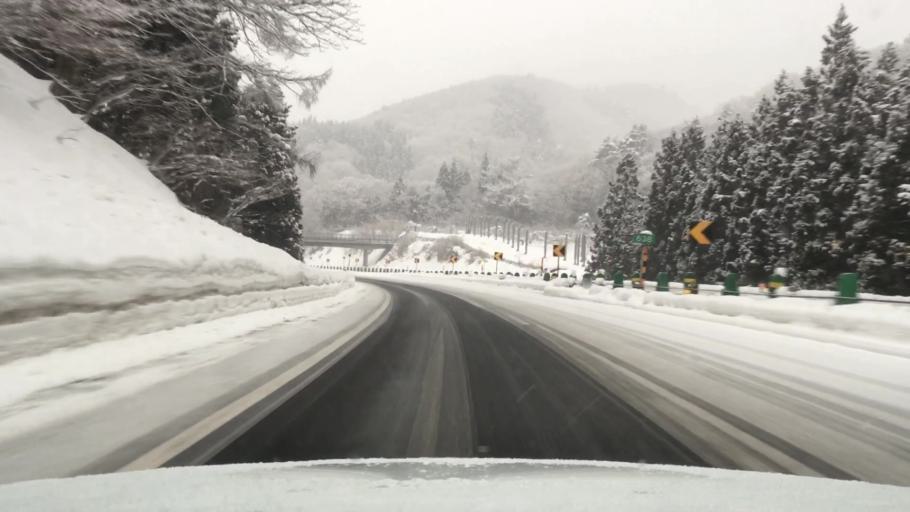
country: JP
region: Aomori
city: Kuroishi
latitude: 40.5228
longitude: 140.5984
